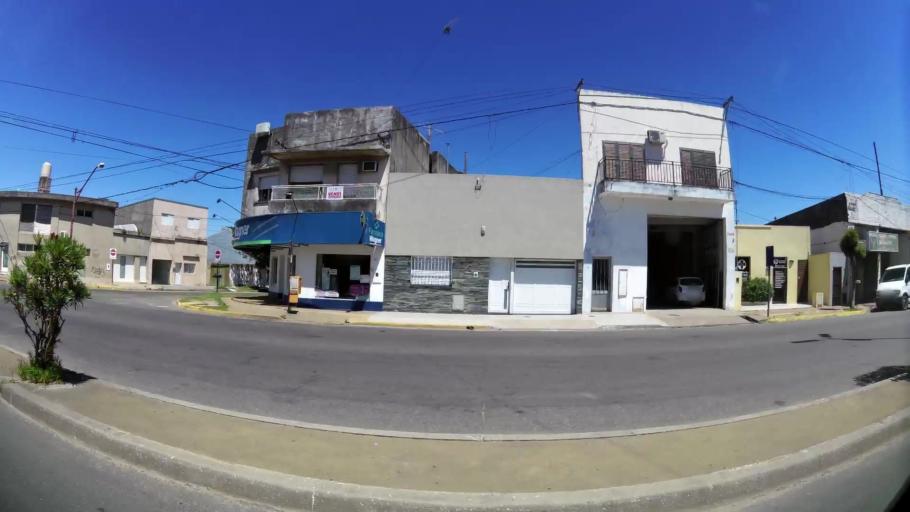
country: AR
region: Santa Fe
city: Santa Fe de la Vera Cruz
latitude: -31.6281
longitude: -60.7051
